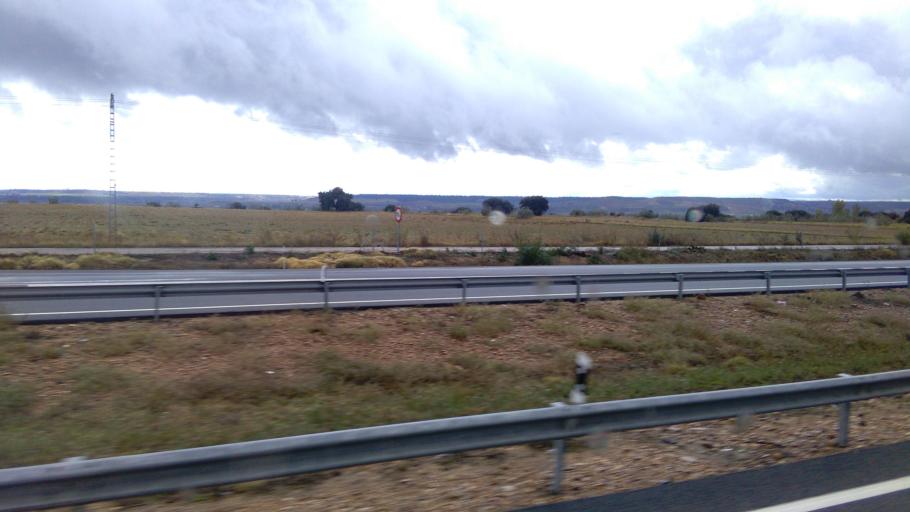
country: ES
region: Castille-La Mancha
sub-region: Province of Toledo
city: Cazalegas
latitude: 39.9883
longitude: -4.7072
